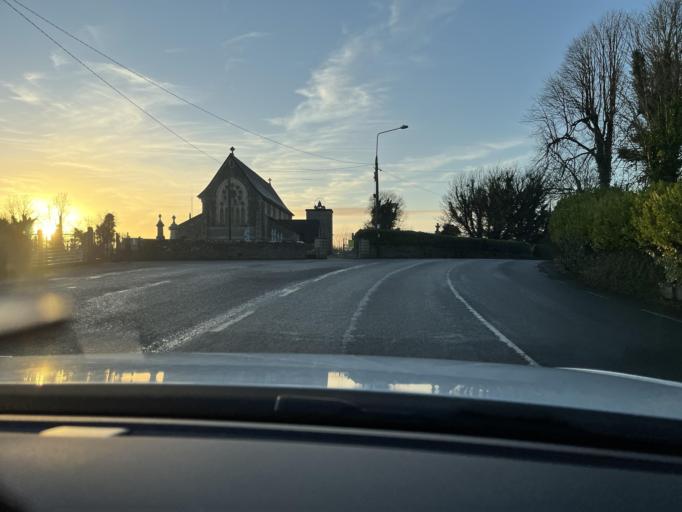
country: IE
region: Ulster
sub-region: An Cabhan
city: Ballyconnell
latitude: 54.0866
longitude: -7.6446
